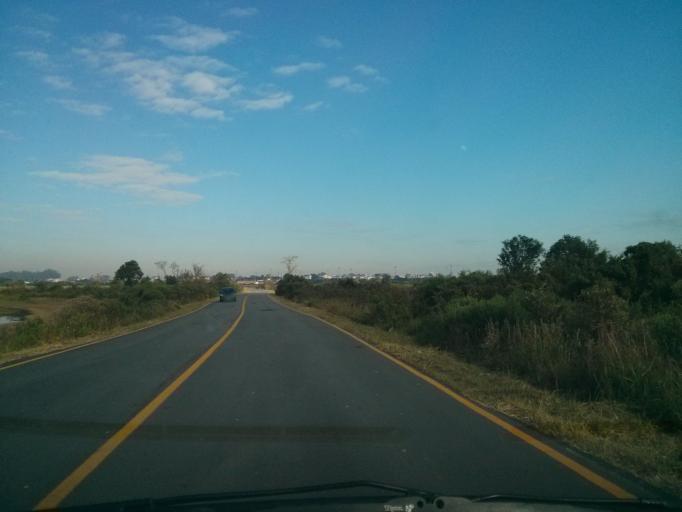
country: BR
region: Parana
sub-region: Sao Jose Dos Pinhais
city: Sao Jose dos Pinhais
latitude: -25.5289
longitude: -49.2215
